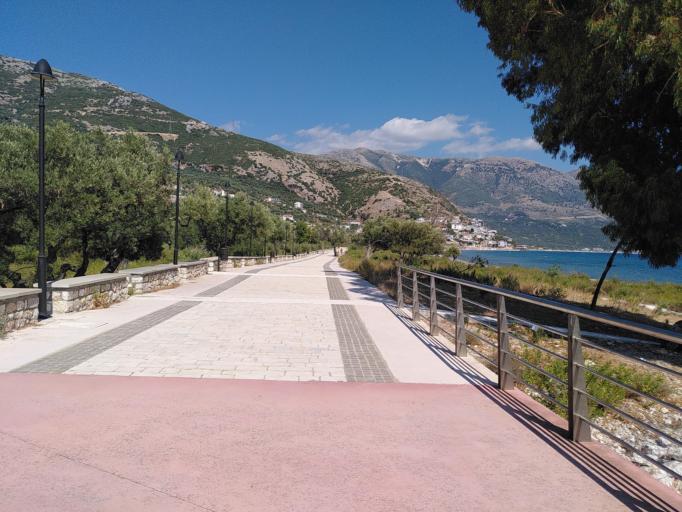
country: AL
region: Vlore
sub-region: Rrethi i Vlores
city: Himare
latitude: 40.0527
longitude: 19.8184
